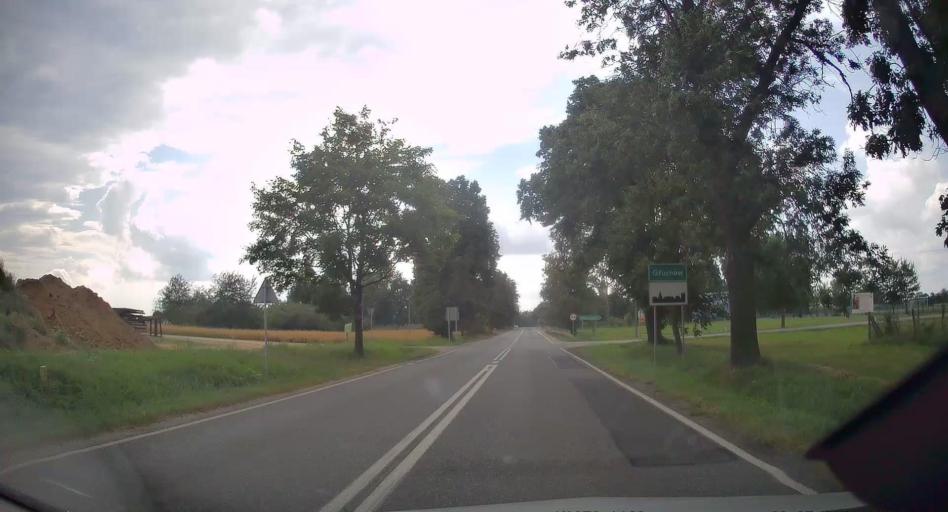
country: PL
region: Lodz Voivodeship
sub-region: Powiat skierniewicki
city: Gluchow
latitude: 51.7789
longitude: 20.0857
